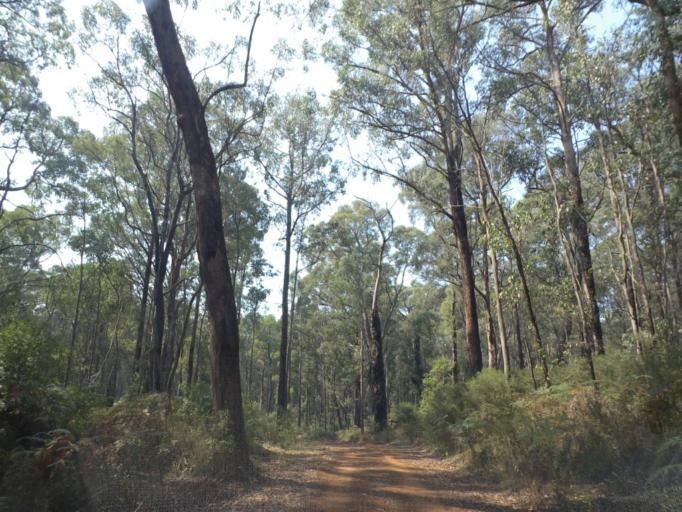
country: AU
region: Victoria
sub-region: Yarra Ranges
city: Millgrove
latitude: -37.5851
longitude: 145.6756
